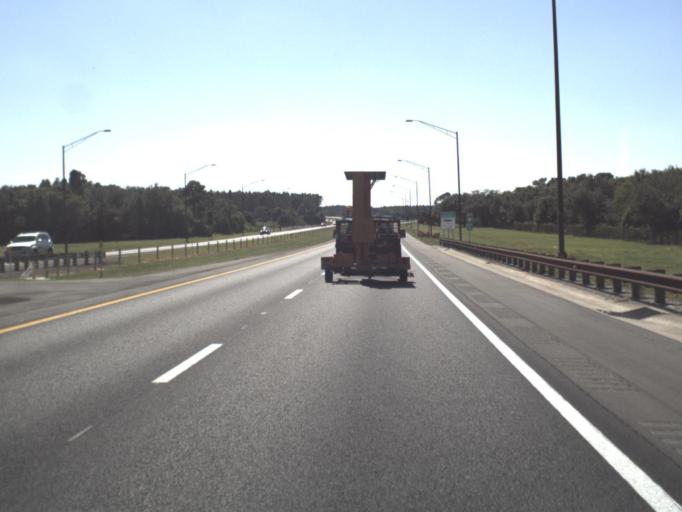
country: US
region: Florida
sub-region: Hillsborough County
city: Cheval
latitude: 28.1405
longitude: -82.5469
